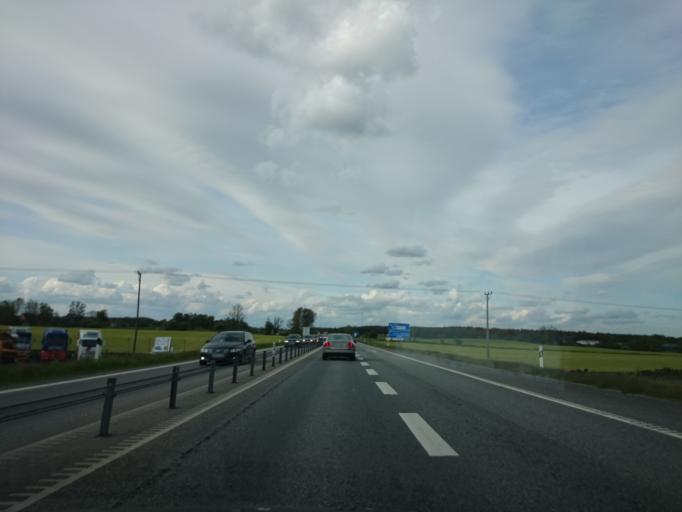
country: SE
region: Skane
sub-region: Kristianstads Kommun
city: Norra Asum
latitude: 55.9530
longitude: 14.0639
